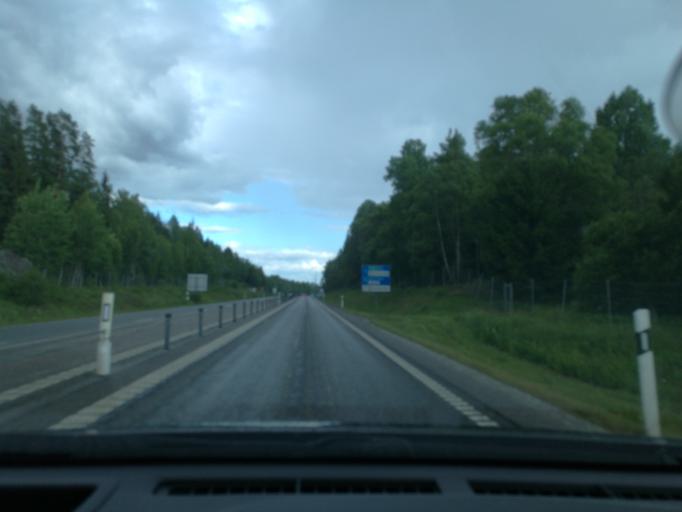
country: SE
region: Vaestmanland
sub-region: Vasteras
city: Vasteras
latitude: 59.6239
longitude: 16.4535
